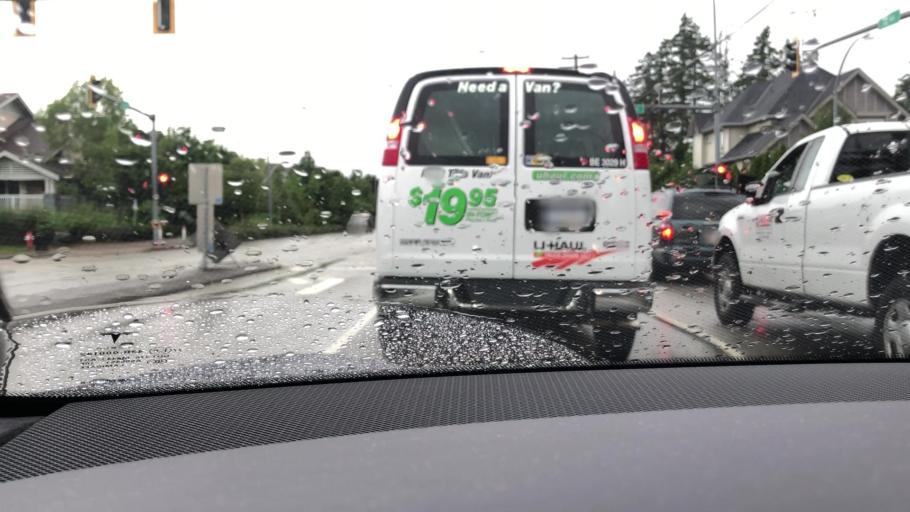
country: CA
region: British Columbia
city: Langley
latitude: 49.1335
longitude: -122.6642
